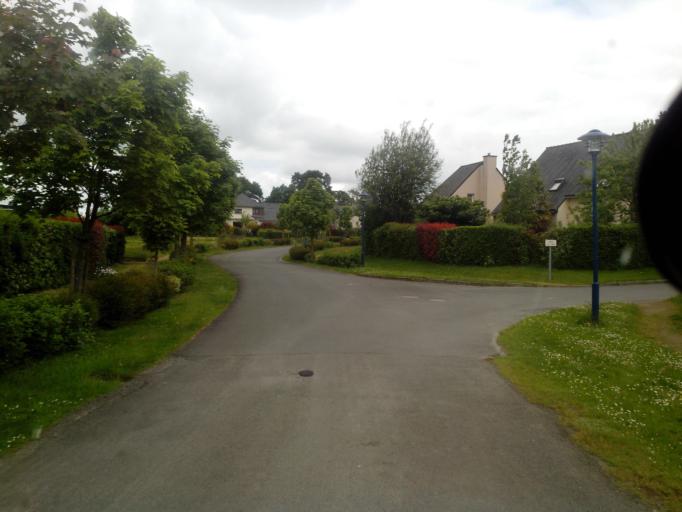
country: FR
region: Brittany
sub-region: Departement d'Ille-et-Vilaine
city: Saint-Medard-sur-Ille
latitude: 48.2506
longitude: -1.6573
